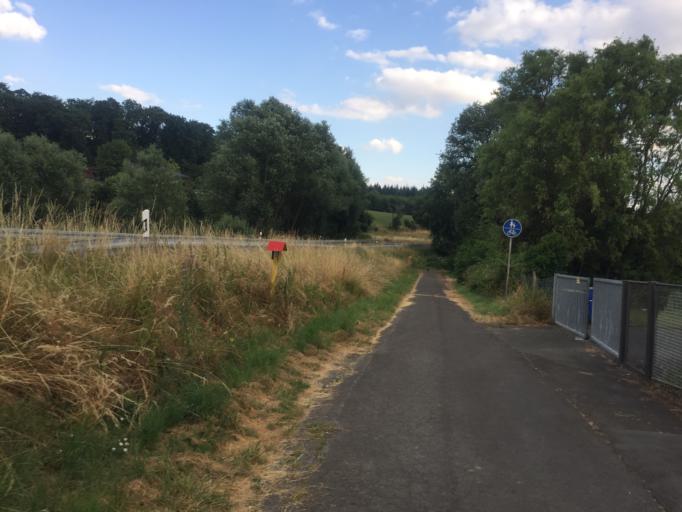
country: DE
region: Hesse
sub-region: Regierungsbezirk Giessen
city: Heuchelheim
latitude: 50.6358
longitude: 8.5977
